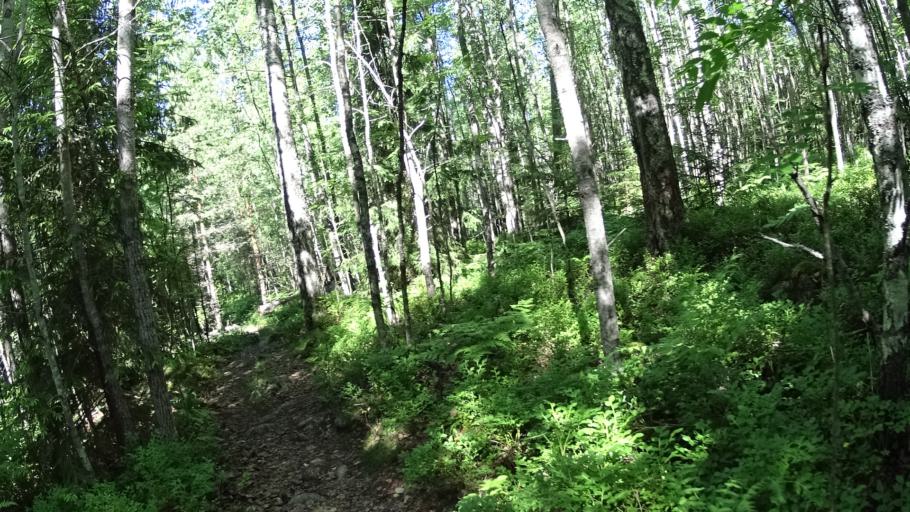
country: FI
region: Uusimaa
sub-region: Helsinki
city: Kilo
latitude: 60.2981
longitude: 24.8384
